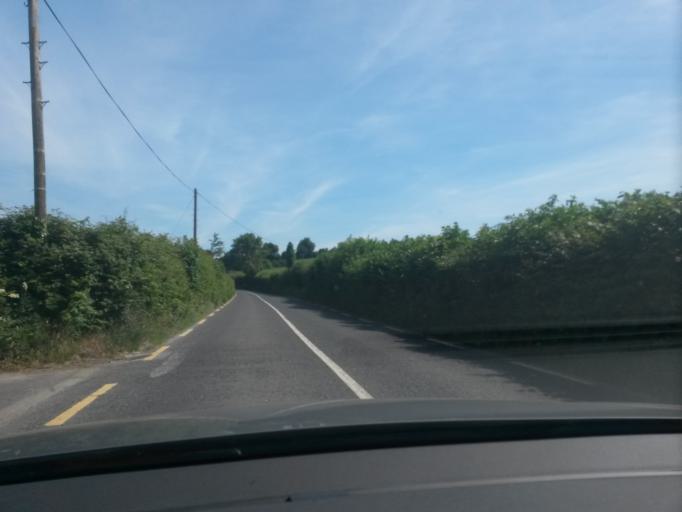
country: IE
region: Leinster
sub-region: Kildare
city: Eadestown
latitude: 53.1978
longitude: -6.5710
